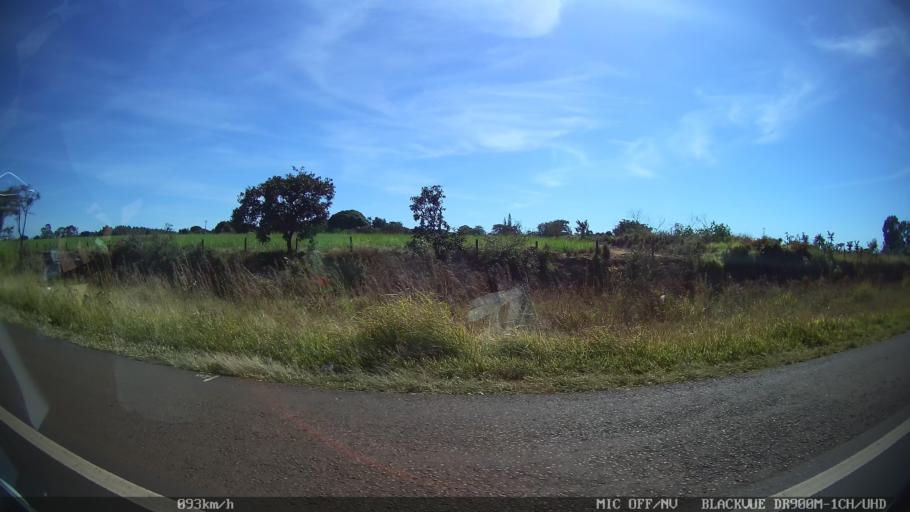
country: BR
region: Sao Paulo
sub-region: Franca
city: Franca
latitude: -20.5481
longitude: -47.4808
